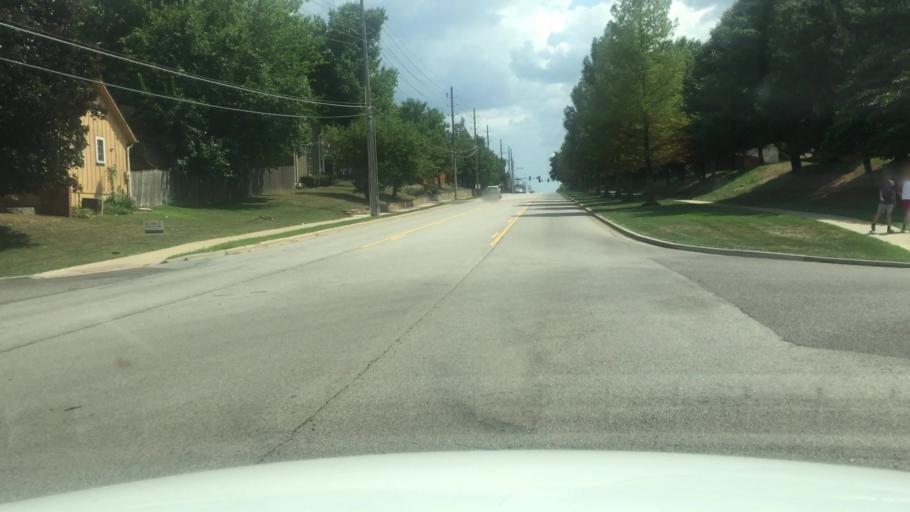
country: US
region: Kansas
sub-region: Johnson County
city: Lenexa
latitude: 38.9593
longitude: -94.7610
